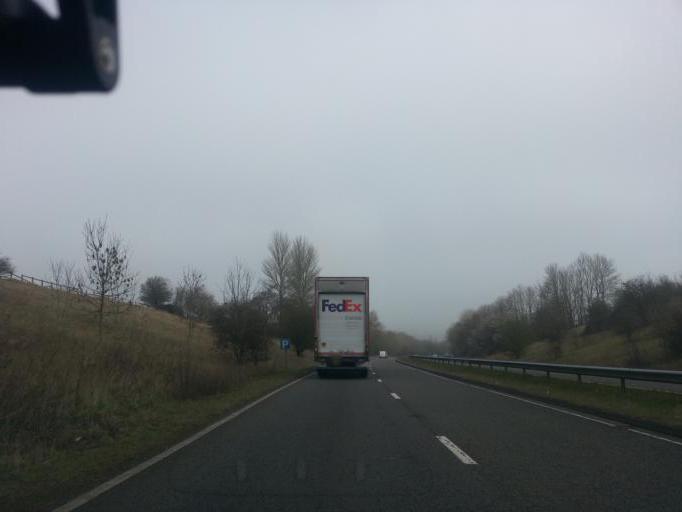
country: GB
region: England
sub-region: Oxfordshire
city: Boars Hill
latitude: 51.7384
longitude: -1.3276
